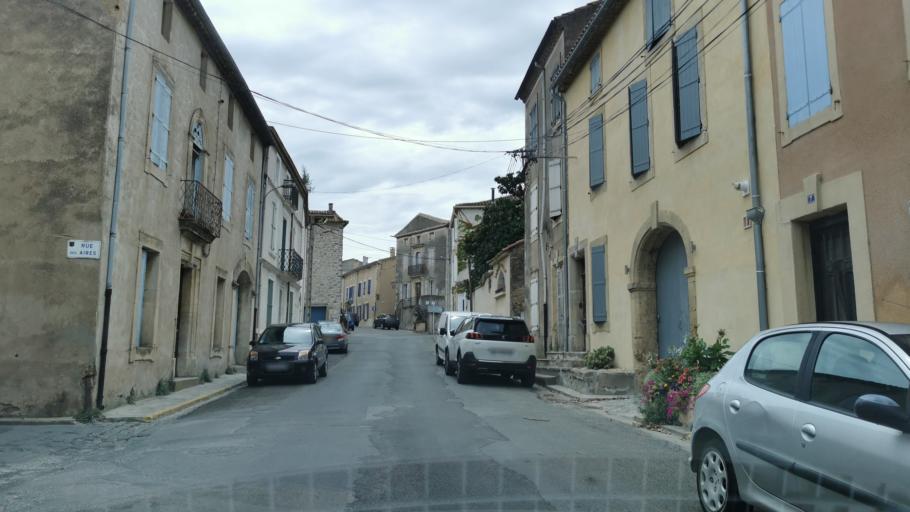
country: FR
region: Languedoc-Roussillon
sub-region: Departement de l'Aude
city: Ginestas
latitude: 43.2690
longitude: 2.8714
